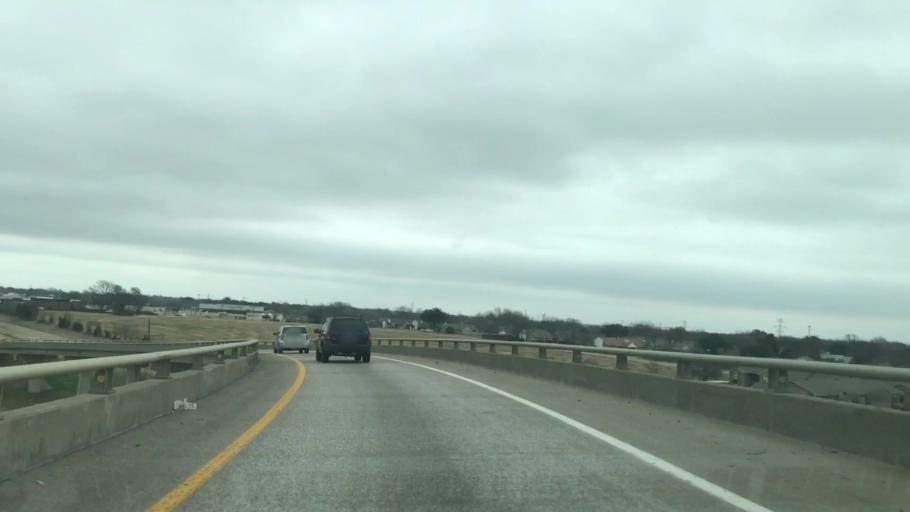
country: US
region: Texas
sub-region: Dallas County
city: Mesquite
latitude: 32.8231
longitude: -96.6288
